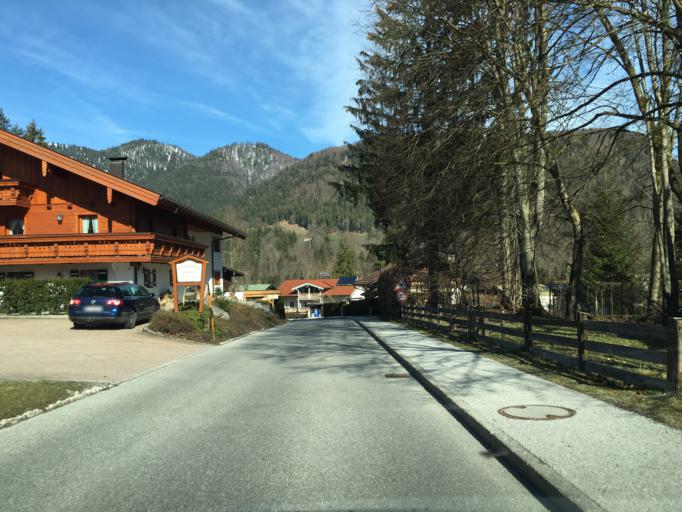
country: DE
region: Bavaria
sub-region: Upper Bavaria
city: Schoenau am Koenigssee
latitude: 47.6117
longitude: 12.9587
